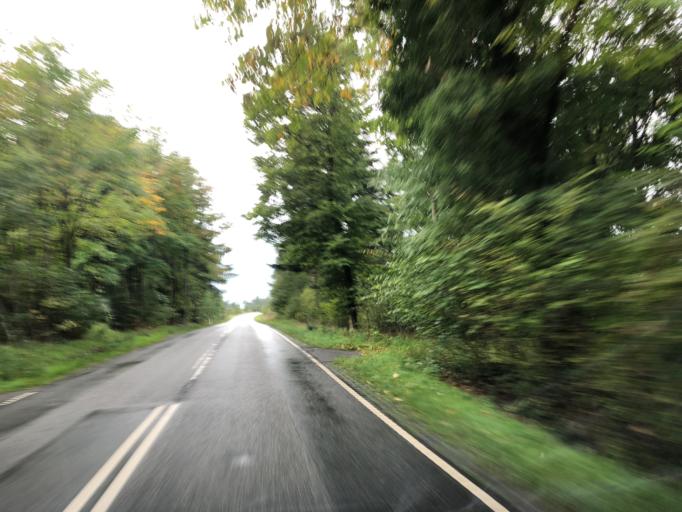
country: DK
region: Central Jutland
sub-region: Ikast-Brande Kommune
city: Brande
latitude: 55.9966
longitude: 9.1966
